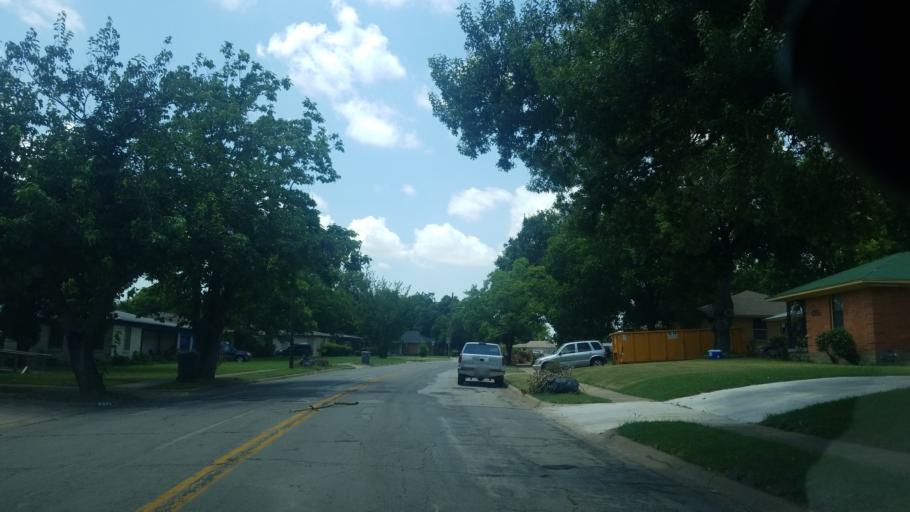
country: US
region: Texas
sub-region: Dallas County
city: Dallas
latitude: 32.7203
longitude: -96.7846
